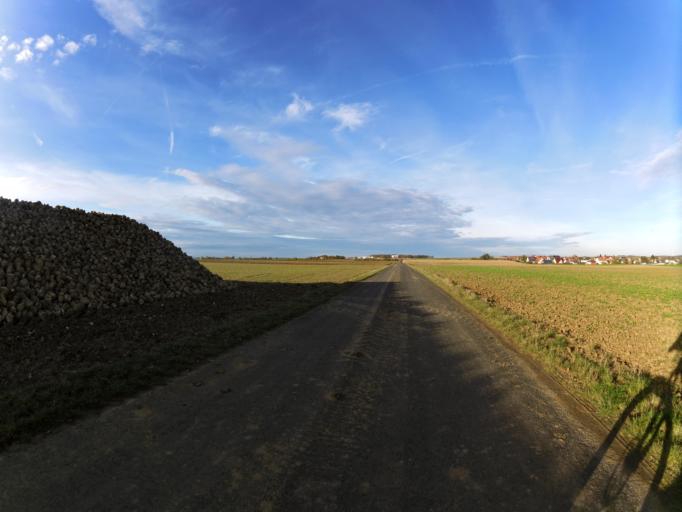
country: DE
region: Bavaria
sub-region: Regierungsbezirk Unterfranken
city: Giebelstadt
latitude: 49.6657
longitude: 9.9514
